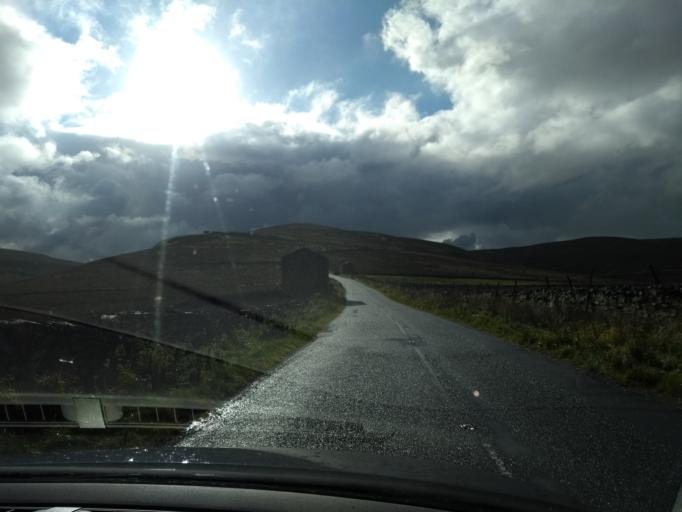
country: GB
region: England
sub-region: Cumbria
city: Kirkby Stephen
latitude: 54.3732
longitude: -2.1817
